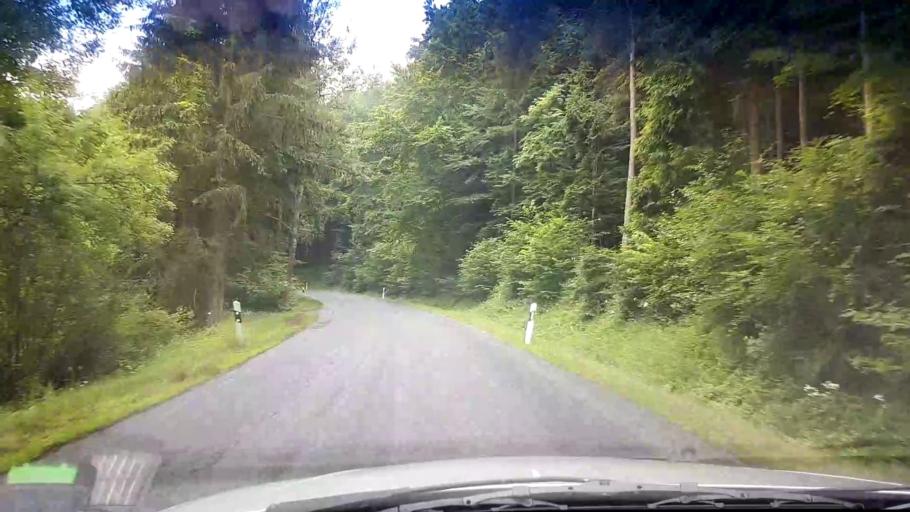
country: DE
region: Bavaria
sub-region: Upper Franconia
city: Wattendorf
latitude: 50.0620
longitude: 11.0836
